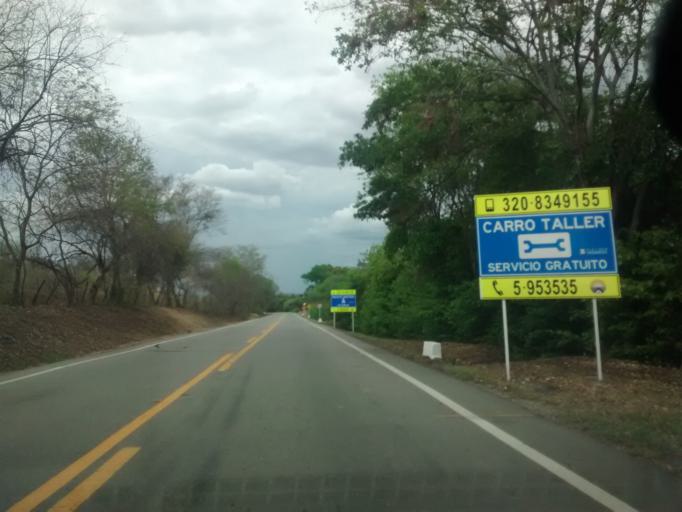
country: CO
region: Cundinamarca
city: Agua de Dios
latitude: 4.4045
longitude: -74.7235
